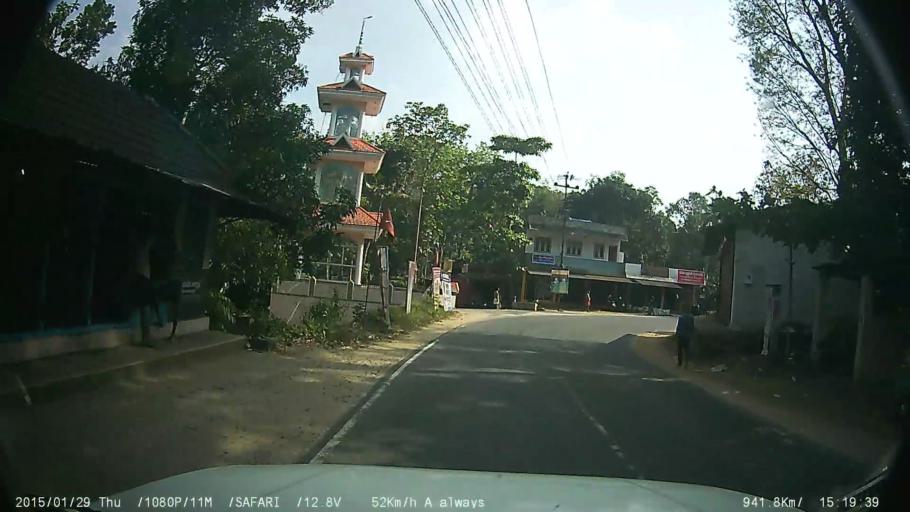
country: IN
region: Kerala
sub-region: Kottayam
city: Palackattumala
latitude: 9.6497
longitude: 76.6125
